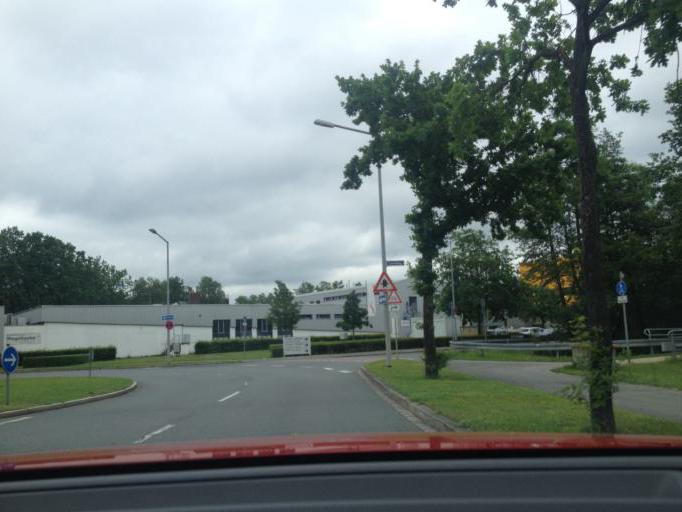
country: DE
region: Bavaria
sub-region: Regierungsbezirk Mittelfranken
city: Nuernberg
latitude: 49.4922
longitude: 11.0835
